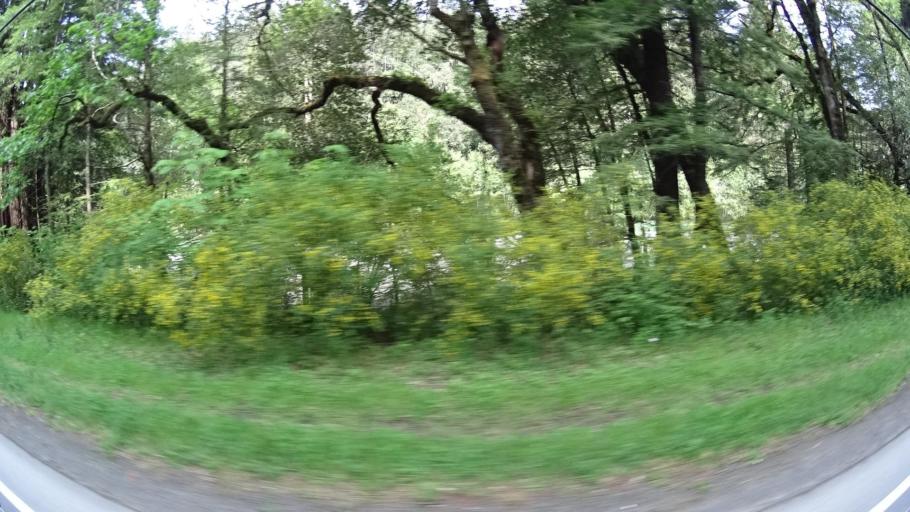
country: US
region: California
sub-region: Humboldt County
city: Redway
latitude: 40.1370
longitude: -123.8152
